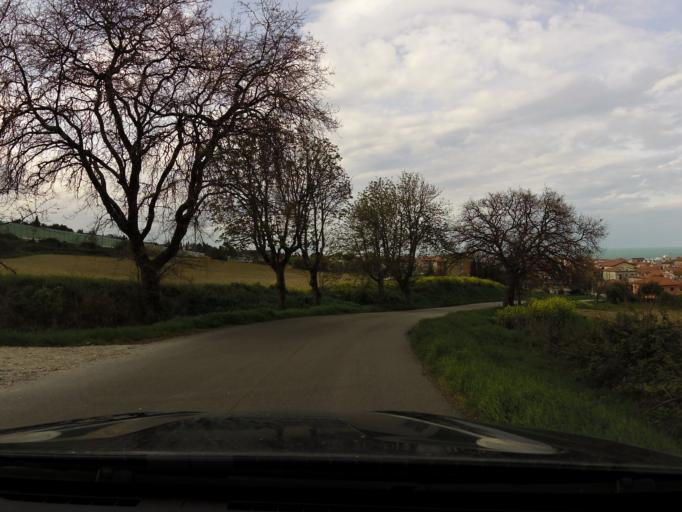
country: IT
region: The Marches
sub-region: Provincia di Macerata
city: Porto Potenza Picena
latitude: 43.3583
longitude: 13.6927
